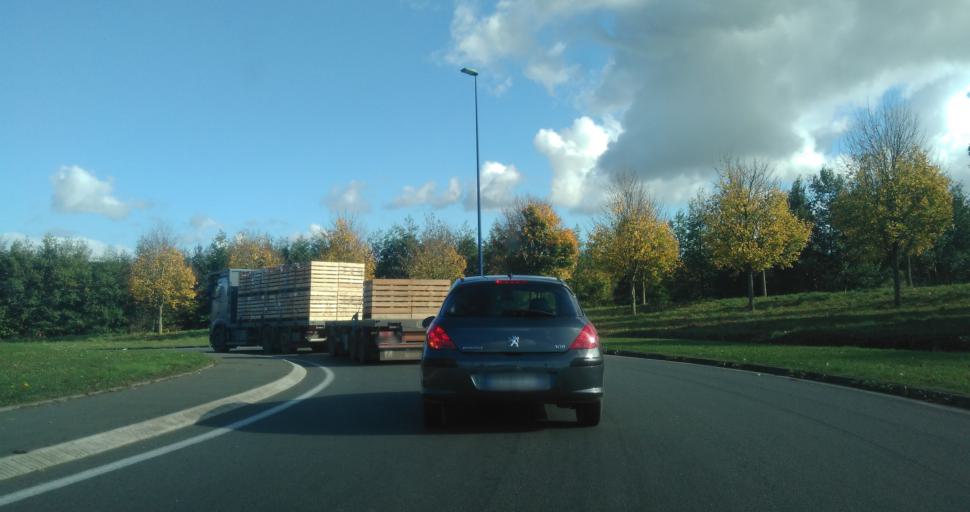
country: FR
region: Nord-Pas-de-Calais
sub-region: Departement du Pas-de-Calais
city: Dainville
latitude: 50.2693
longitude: 2.7117
